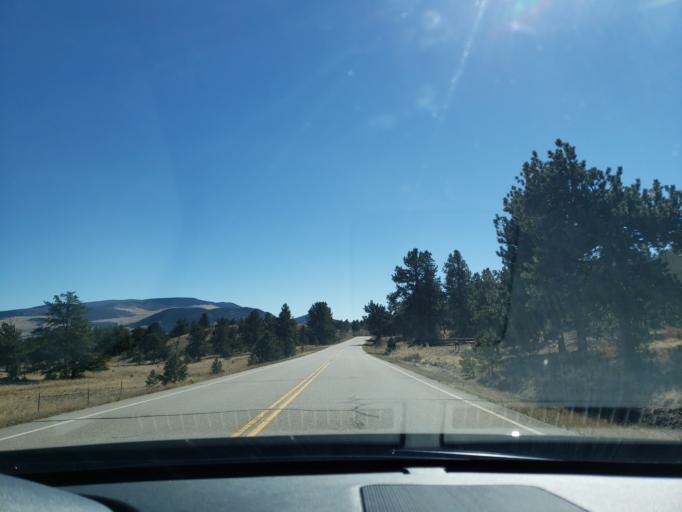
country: US
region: Colorado
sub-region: Chaffee County
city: Buena Vista
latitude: 38.8894
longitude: -105.6850
